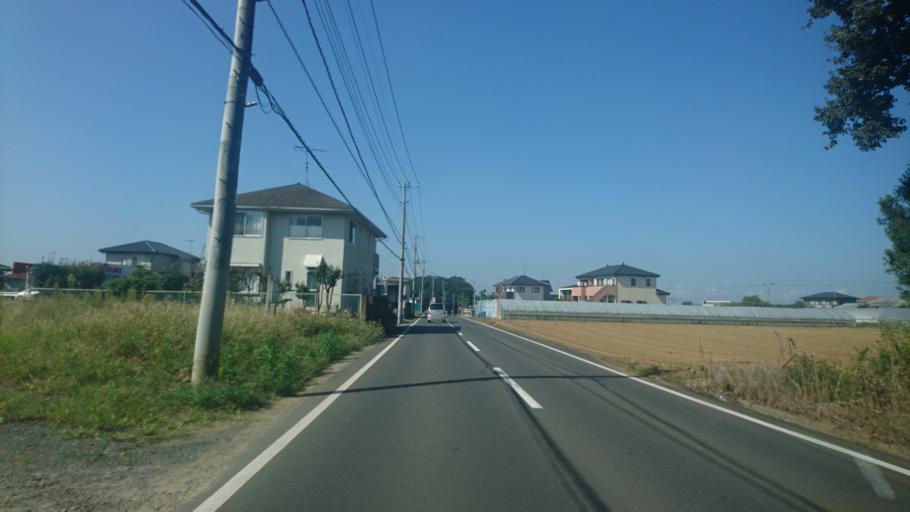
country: JP
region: Ibaraki
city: Shimodate
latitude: 36.2756
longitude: 139.9553
